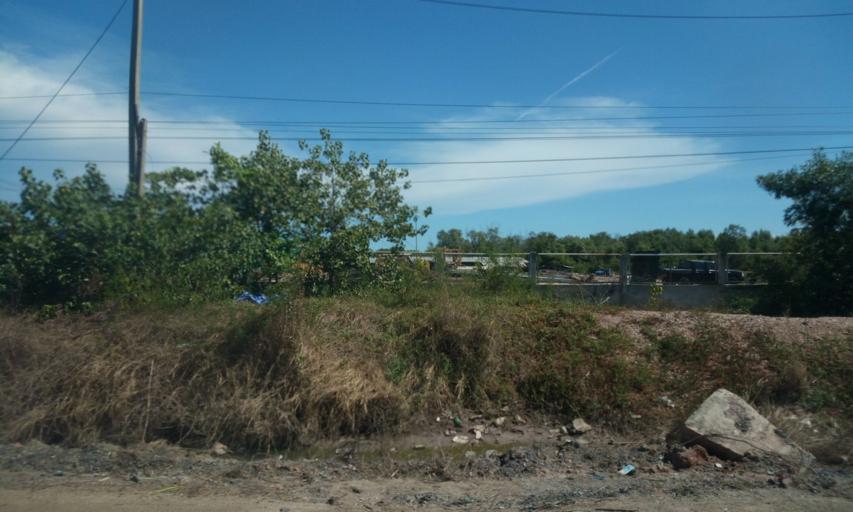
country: TH
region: Samut Prakan
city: Bang Bo District
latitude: 13.5020
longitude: 100.7633
